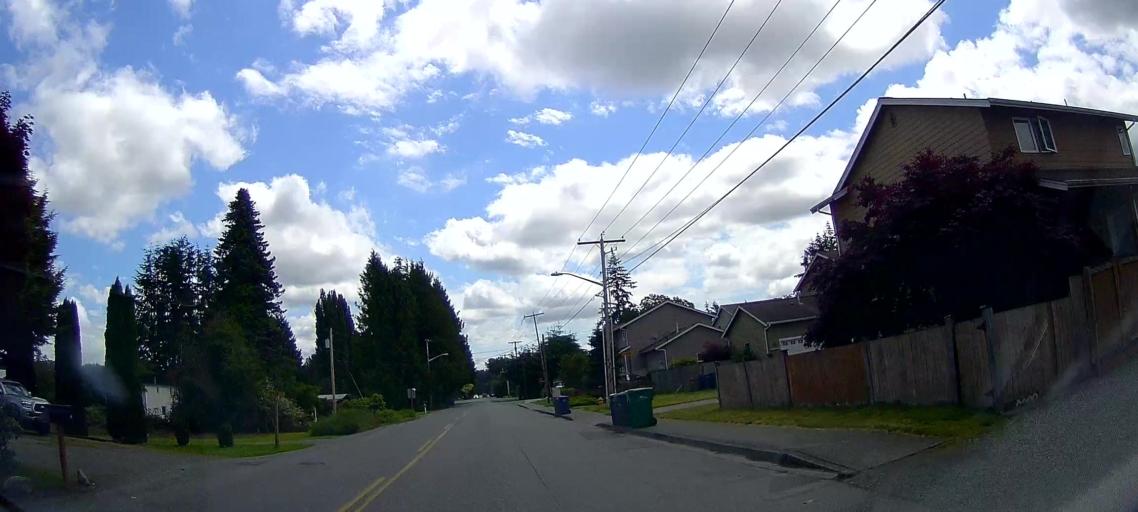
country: US
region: Washington
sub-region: Skagit County
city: Burlington
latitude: 48.4763
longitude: -122.3085
